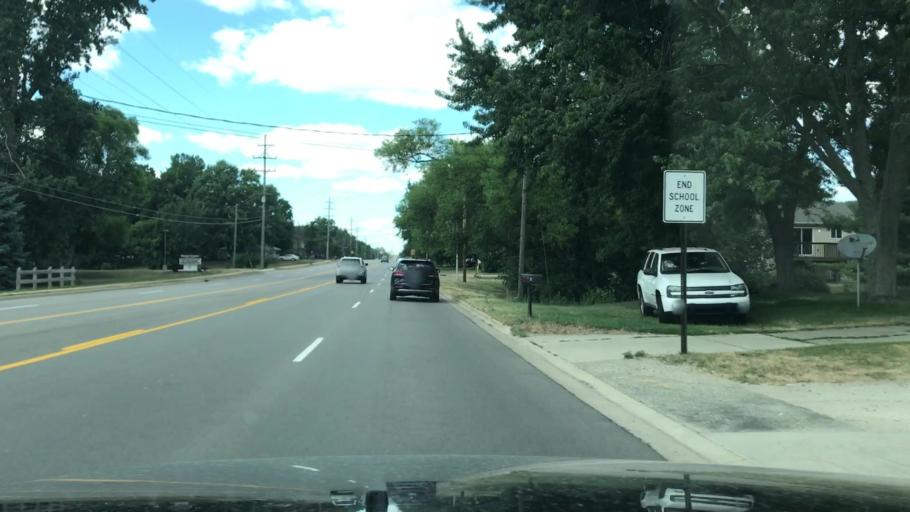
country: US
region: Michigan
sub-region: Kent County
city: Byron Center
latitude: 42.8308
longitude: -85.7227
